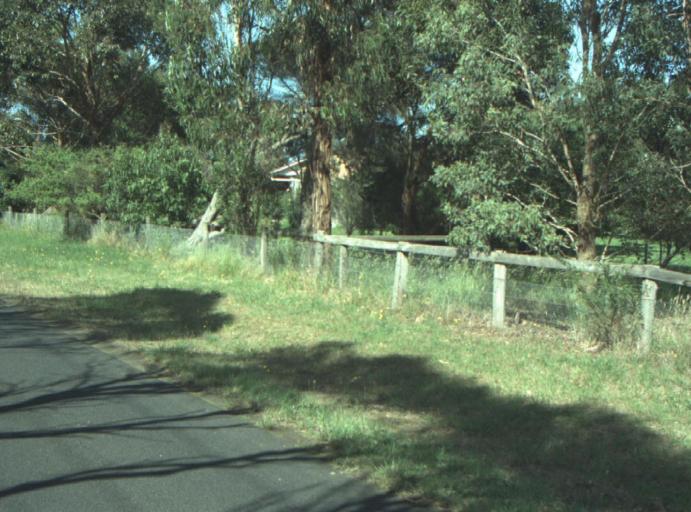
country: AU
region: Victoria
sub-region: Greater Geelong
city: Clifton Springs
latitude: -38.2346
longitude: 144.5788
